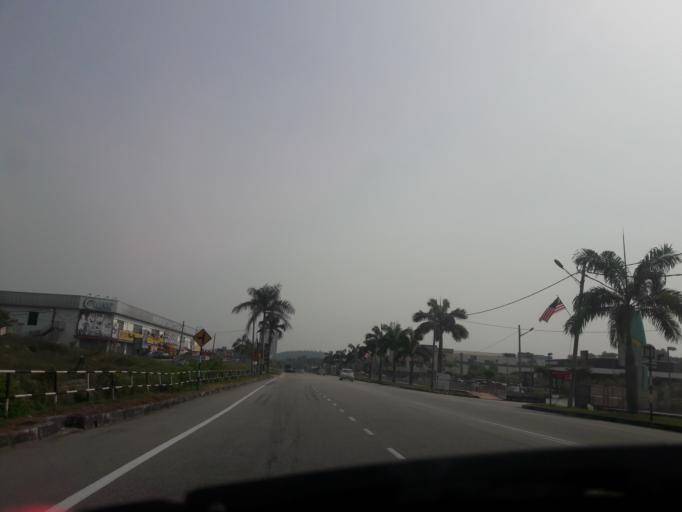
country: MY
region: Kedah
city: Kulim
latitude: 5.3822
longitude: 100.5451
